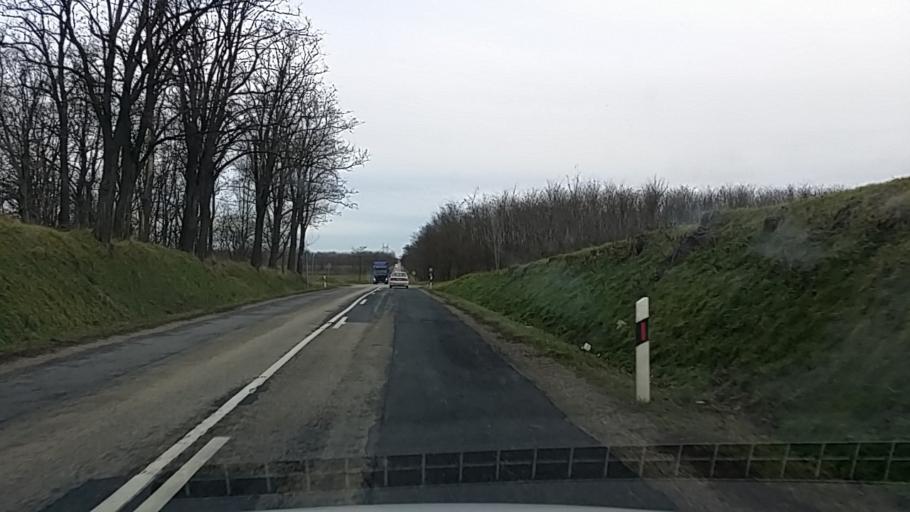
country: HU
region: Veszprem
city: Papa
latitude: 47.3352
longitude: 17.5177
